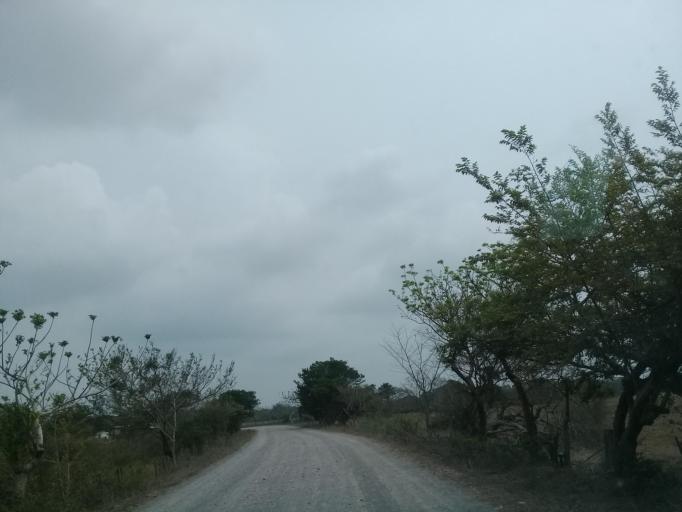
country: MX
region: Veracruz
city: El Tejar
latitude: 19.0596
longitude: -96.1980
